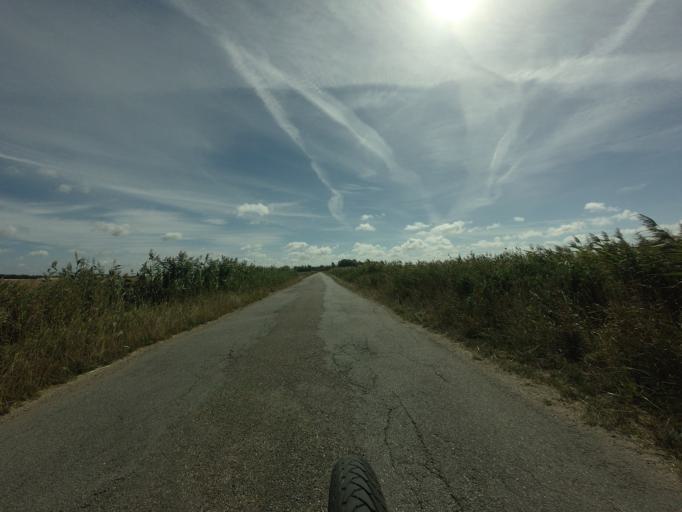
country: DK
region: North Denmark
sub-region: Hjorring Kommune
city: Vra
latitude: 57.3410
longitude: 9.8024
